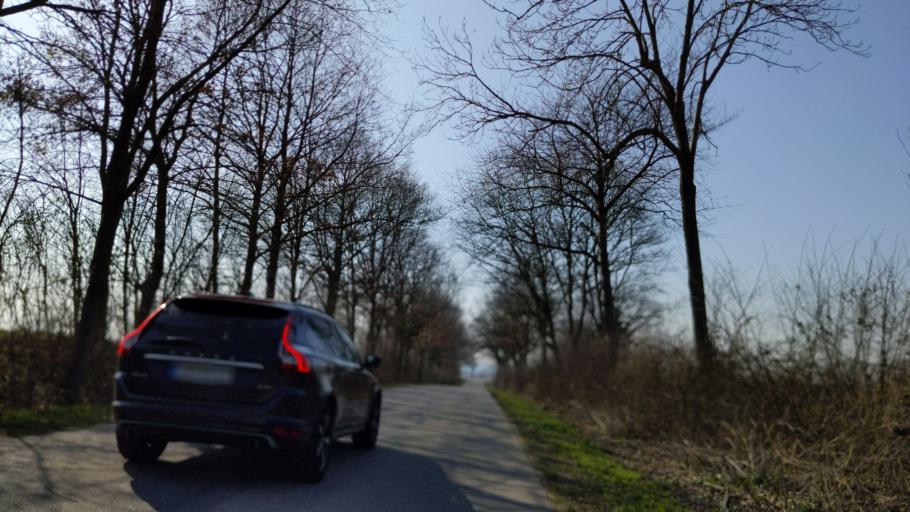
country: DE
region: Schleswig-Holstein
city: Altenkrempe
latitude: 54.1314
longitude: 10.8521
